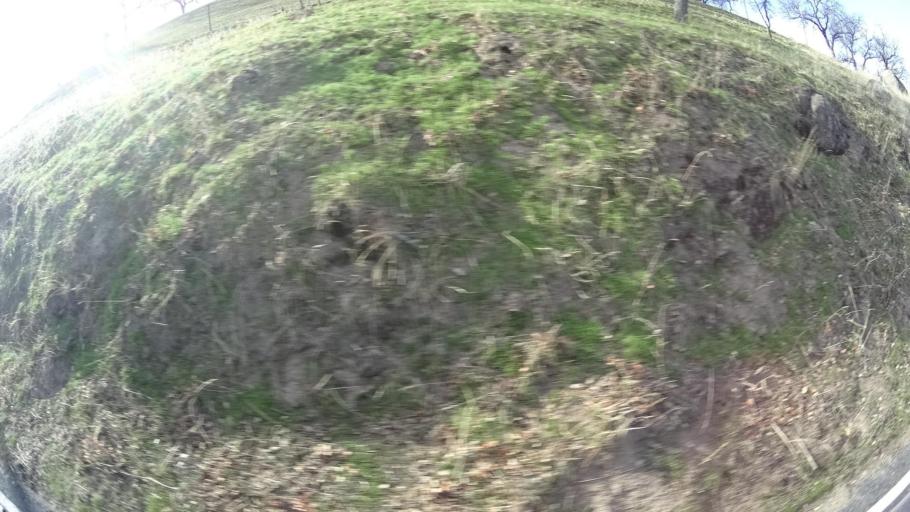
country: US
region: California
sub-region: Kern County
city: Alta Sierra
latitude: 35.6282
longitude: -118.8115
